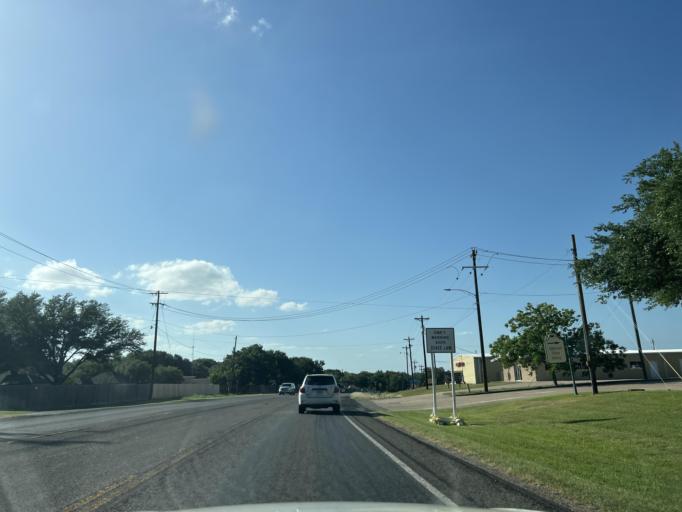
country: US
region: Texas
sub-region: Washington County
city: Brenham
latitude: 30.1636
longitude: -96.3799
